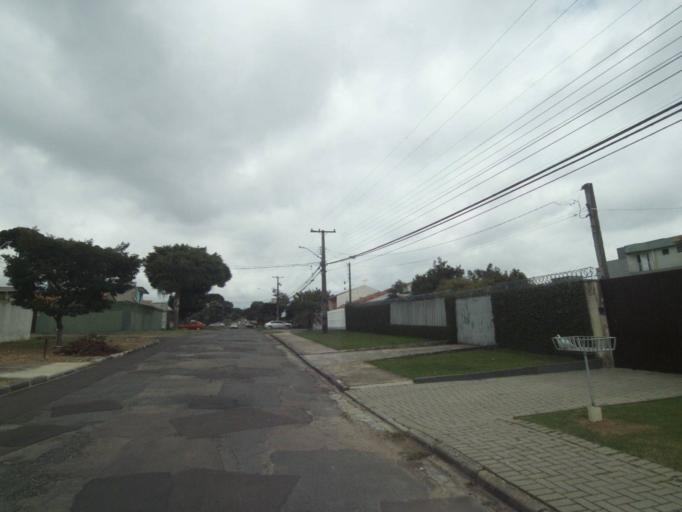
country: BR
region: Parana
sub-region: Pinhais
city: Pinhais
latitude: -25.4566
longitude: -49.2161
